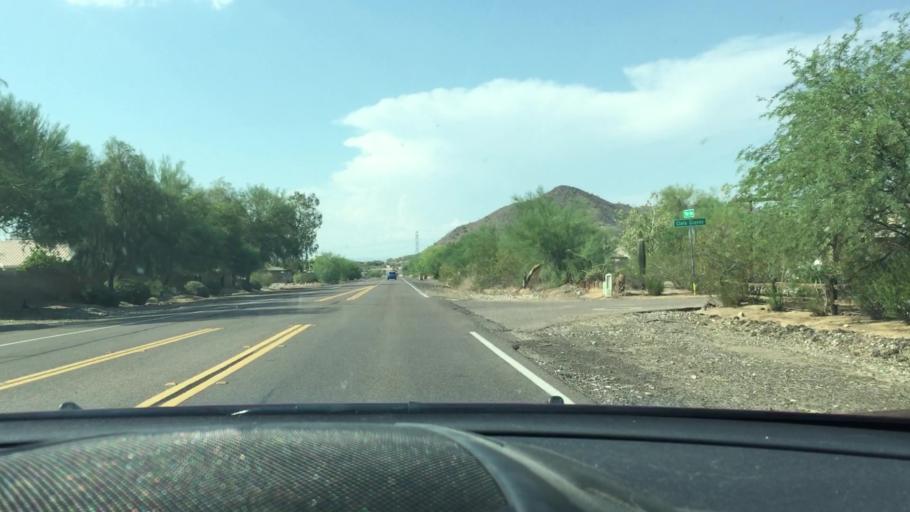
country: US
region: Arizona
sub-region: Maricopa County
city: Sun City West
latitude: 33.7007
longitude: -112.2550
